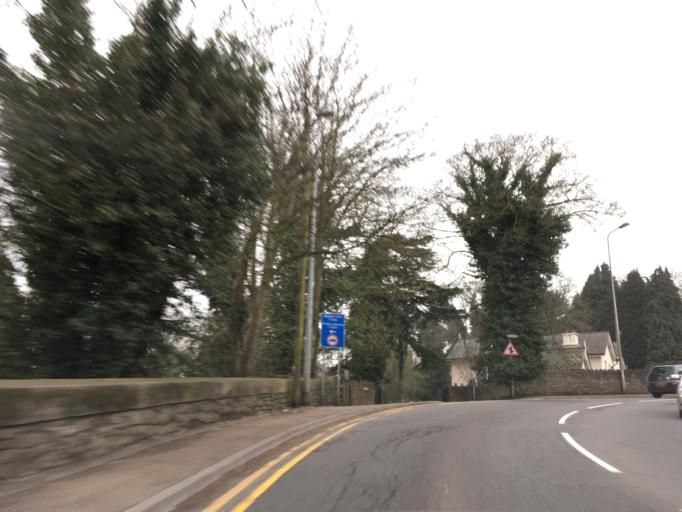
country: GB
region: Wales
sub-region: Monmouthshire
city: Chepstow
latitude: 51.6384
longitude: -2.6784
